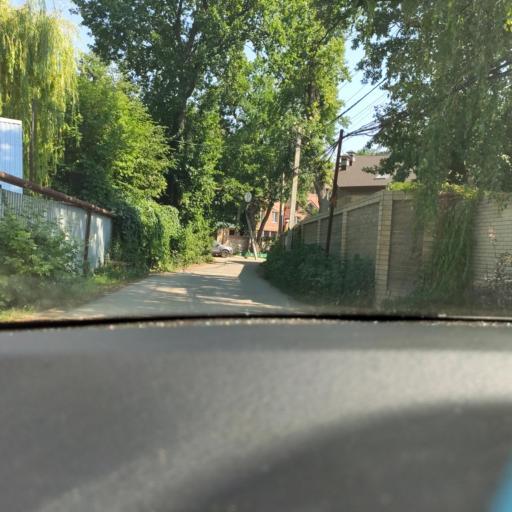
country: RU
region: Samara
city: Samara
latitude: 53.2861
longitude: 50.1951
